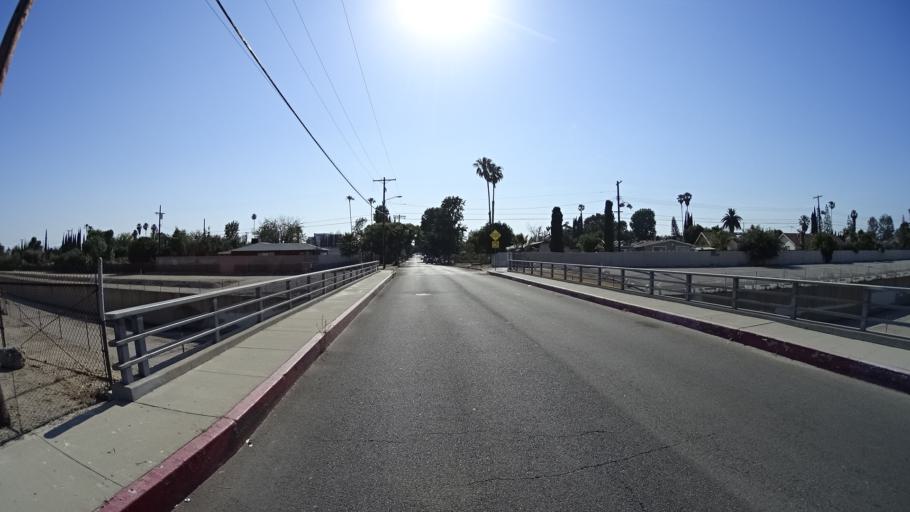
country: US
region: California
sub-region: Los Angeles County
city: Van Nuys
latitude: 34.2198
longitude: -118.4230
